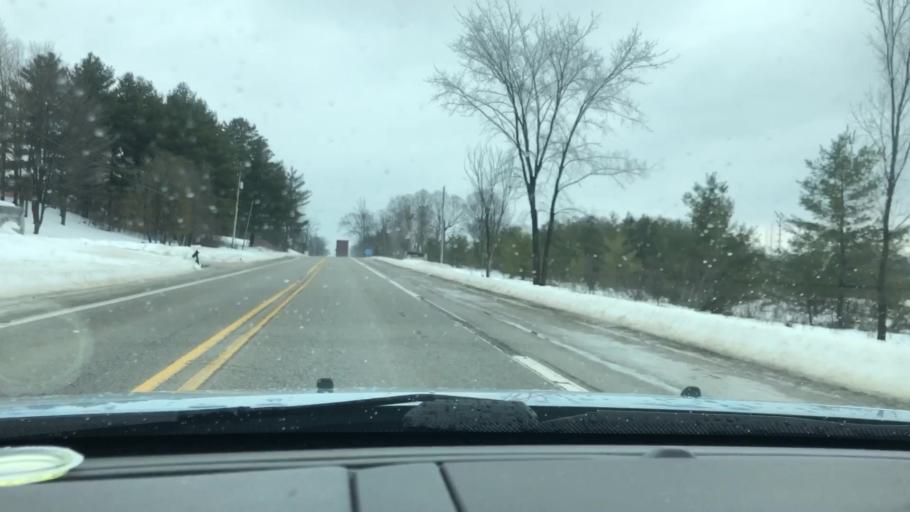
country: US
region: Michigan
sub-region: Charlevoix County
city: East Jordan
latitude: 45.1415
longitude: -85.1398
